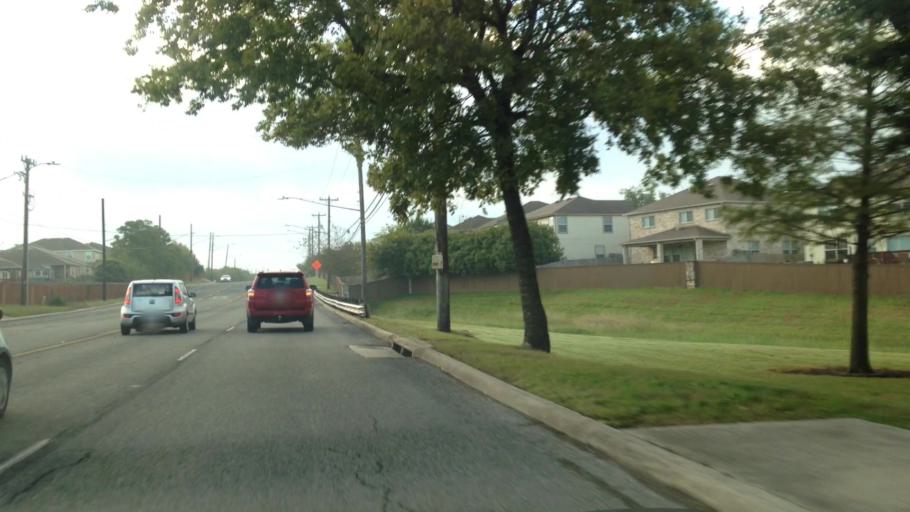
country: US
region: Texas
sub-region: Bexar County
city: Live Oak
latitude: 29.5583
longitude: -98.3595
